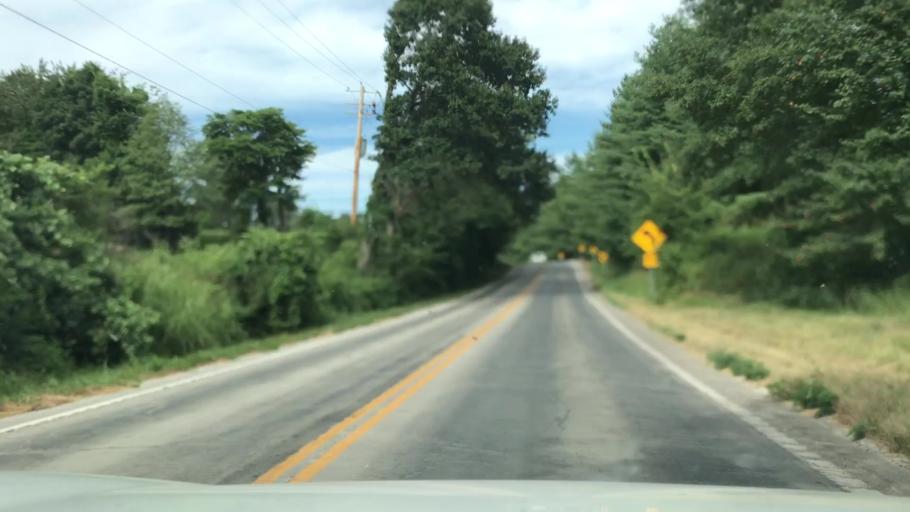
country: US
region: Missouri
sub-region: Saint Charles County
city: Weldon Spring
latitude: 38.6537
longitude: -90.7743
